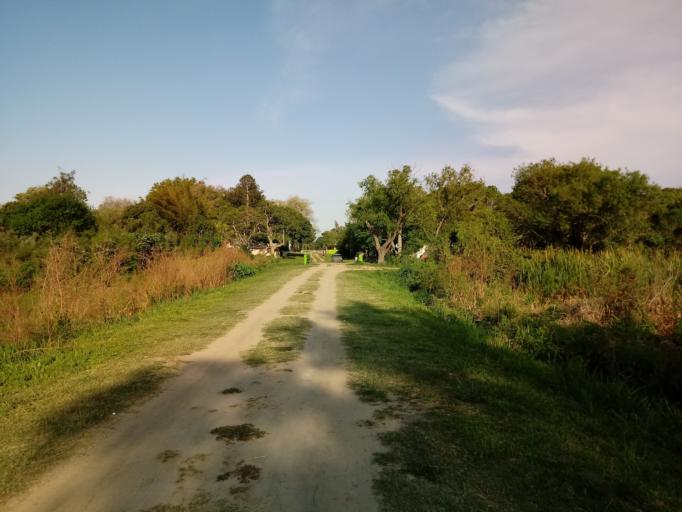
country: AR
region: Corrientes
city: San Luis del Palmar
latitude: -27.4556
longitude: -58.6572
